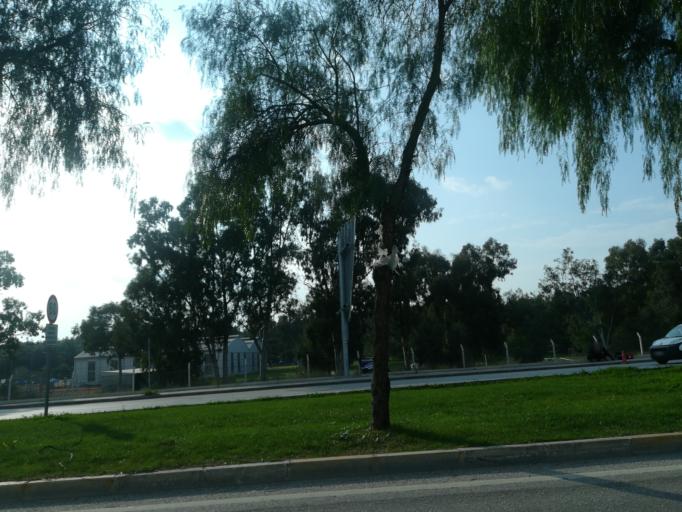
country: TR
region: Adana
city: Adana
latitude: 37.0291
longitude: 35.3452
